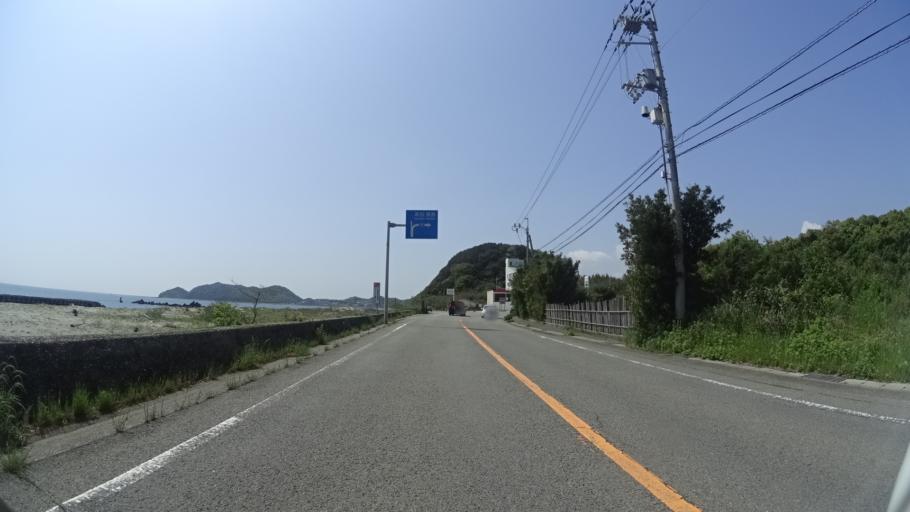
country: JP
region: Tokushima
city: Narutocho-mitsuishi
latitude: 34.1970
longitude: 134.6255
